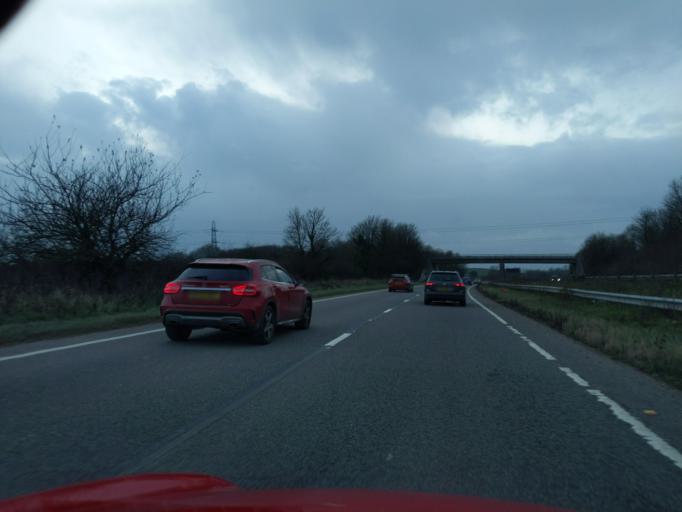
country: GB
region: England
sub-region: Devon
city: Yealmpton
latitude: 50.3804
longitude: -4.0006
